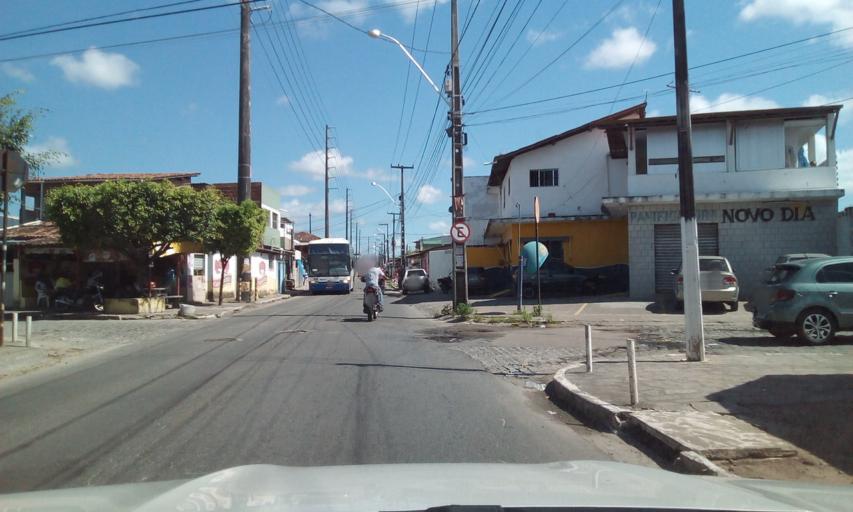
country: BR
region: Paraiba
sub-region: Joao Pessoa
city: Joao Pessoa
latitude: -7.1568
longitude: -34.8775
